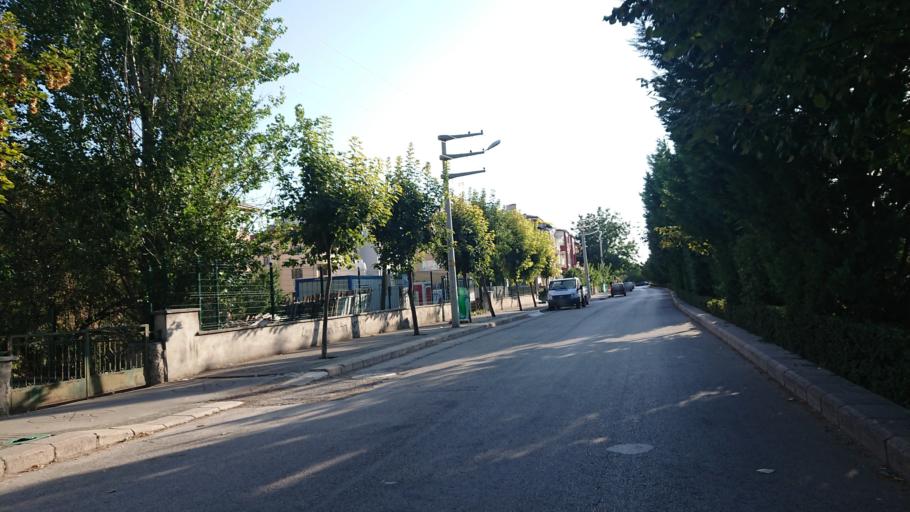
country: TR
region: Eskisehir
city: Eskisehir
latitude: 39.7671
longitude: 30.4913
